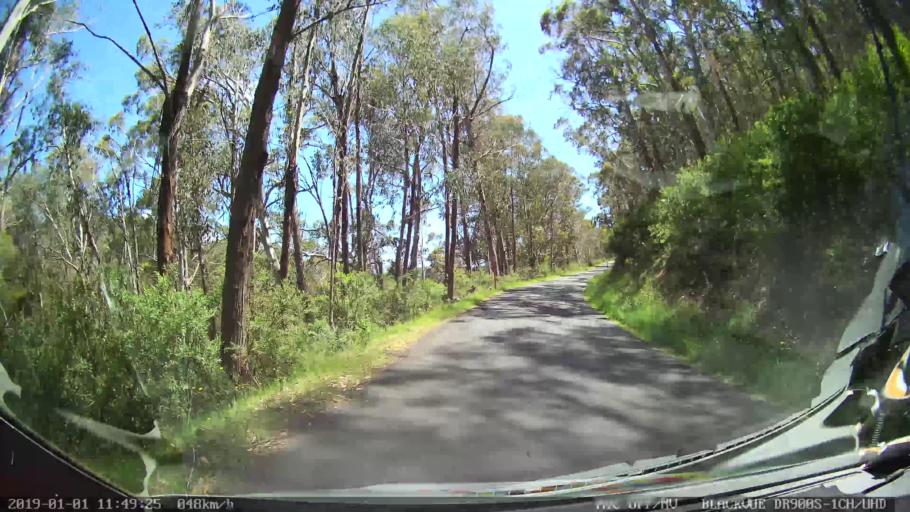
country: AU
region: New South Wales
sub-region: Snowy River
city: Jindabyne
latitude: -35.8939
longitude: 148.4132
